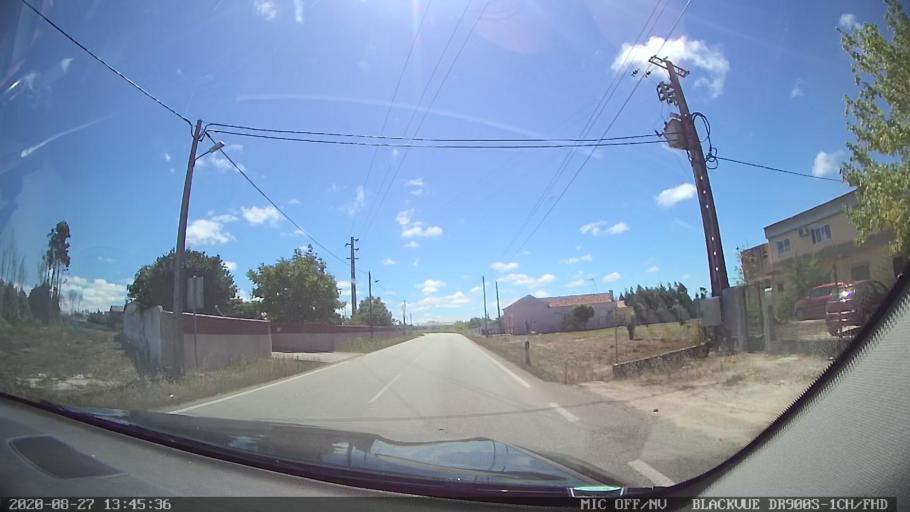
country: PT
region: Coimbra
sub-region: Mira
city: Mira
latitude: 40.4030
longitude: -8.7356
